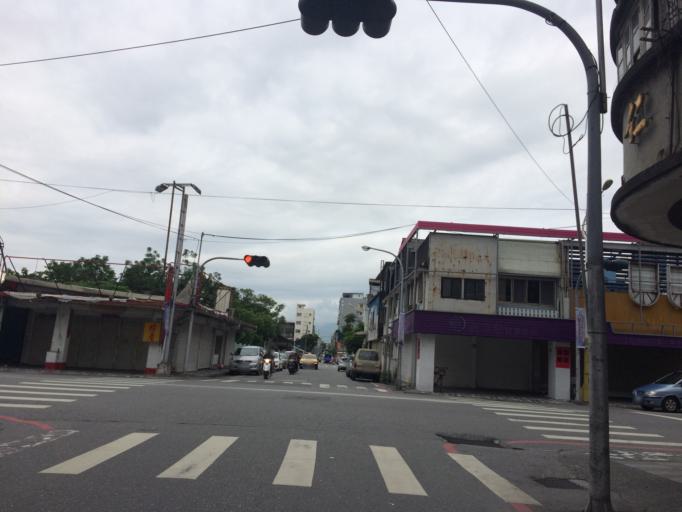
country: TW
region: Taiwan
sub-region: Hualien
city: Hualian
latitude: 23.9756
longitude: 121.6108
